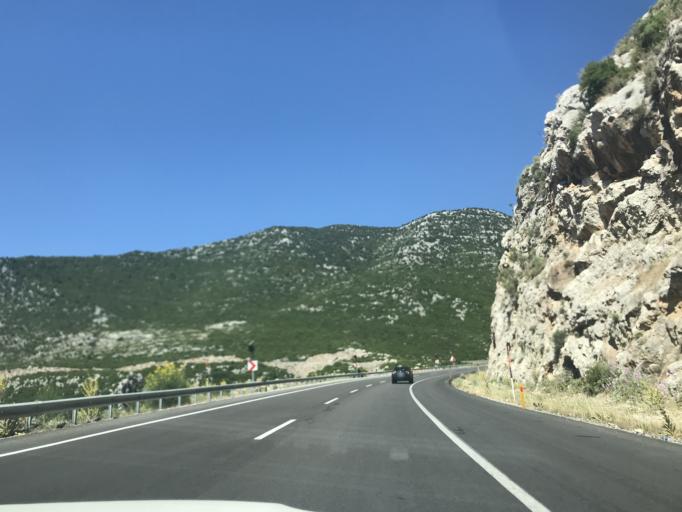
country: TR
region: Antalya
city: Dagbeli
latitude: 37.1629
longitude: 30.5063
